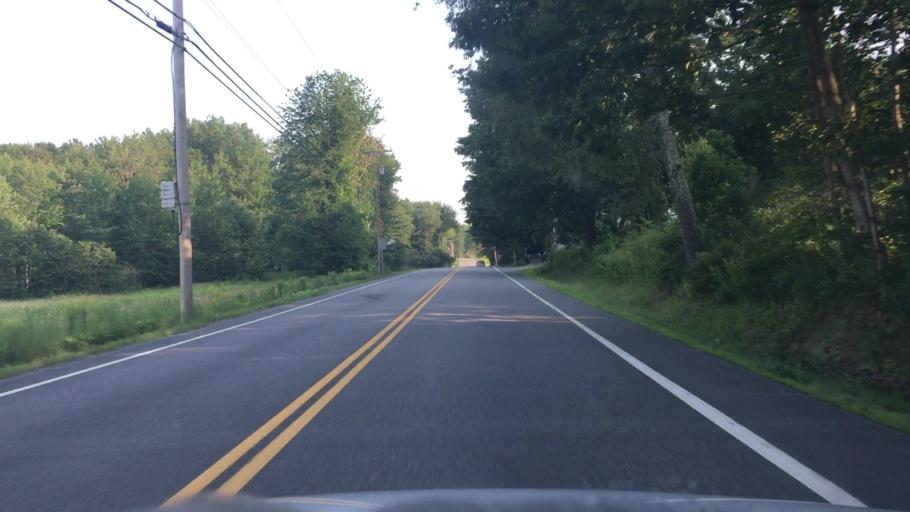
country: US
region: Maine
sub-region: Cumberland County
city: Freeport
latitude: 43.8866
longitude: -70.0937
